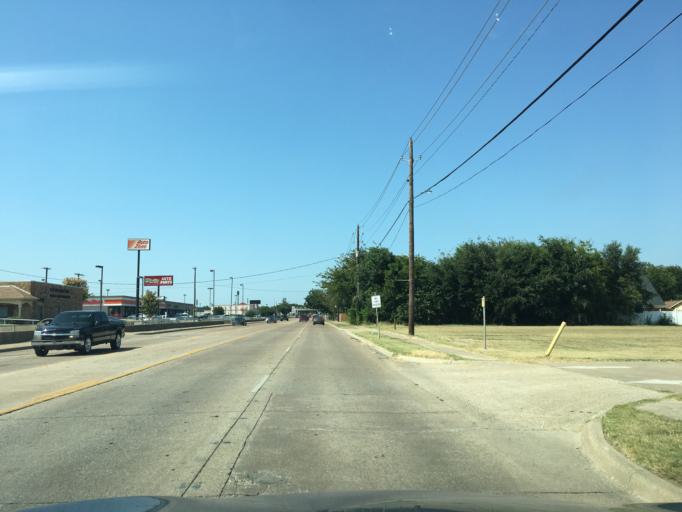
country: US
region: Texas
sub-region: Tarrant County
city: Forest Hill
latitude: 32.6558
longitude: -97.2699
